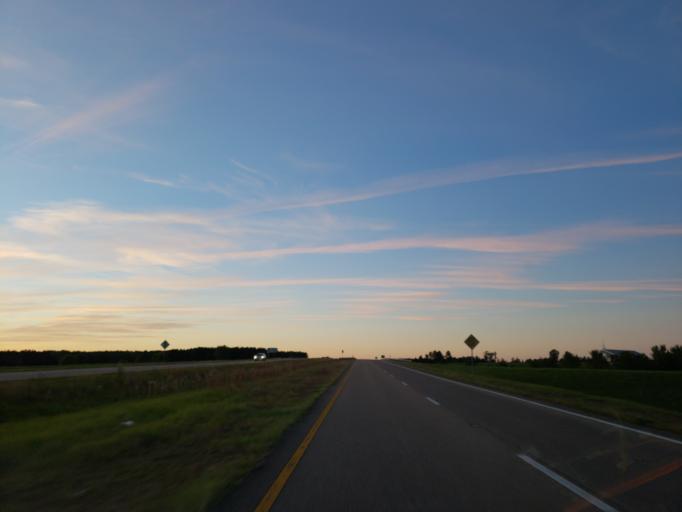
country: US
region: Mississippi
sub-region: Wayne County
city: Waynesboro
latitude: 31.7056
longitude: -88.6245
